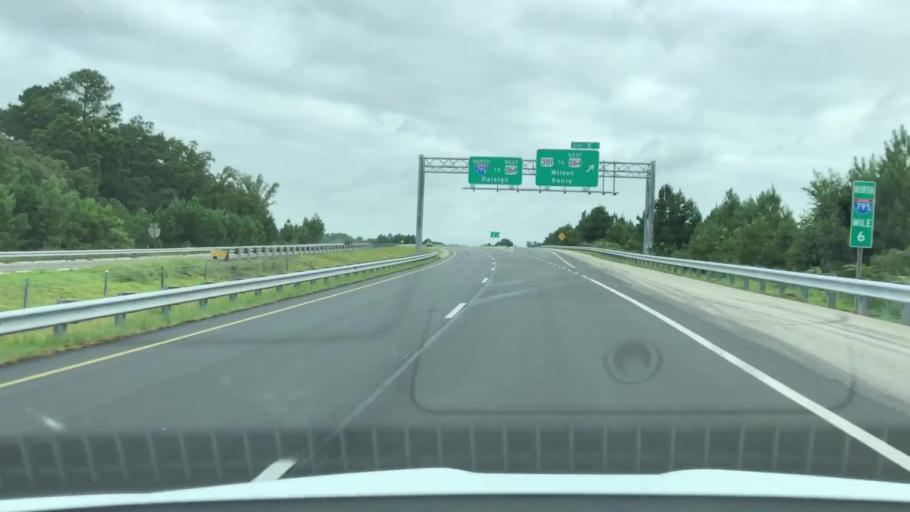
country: US
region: North Carolina
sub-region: Wilson County
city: Lucama
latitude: 35.6637
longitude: -77.9555
